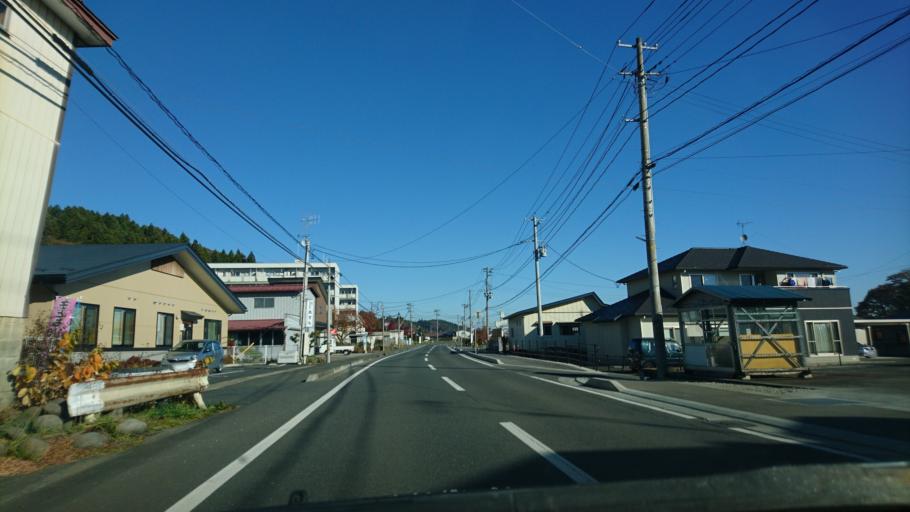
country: JP
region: Iwate
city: Mizusawa
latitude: 39.0626
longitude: 141.1255
